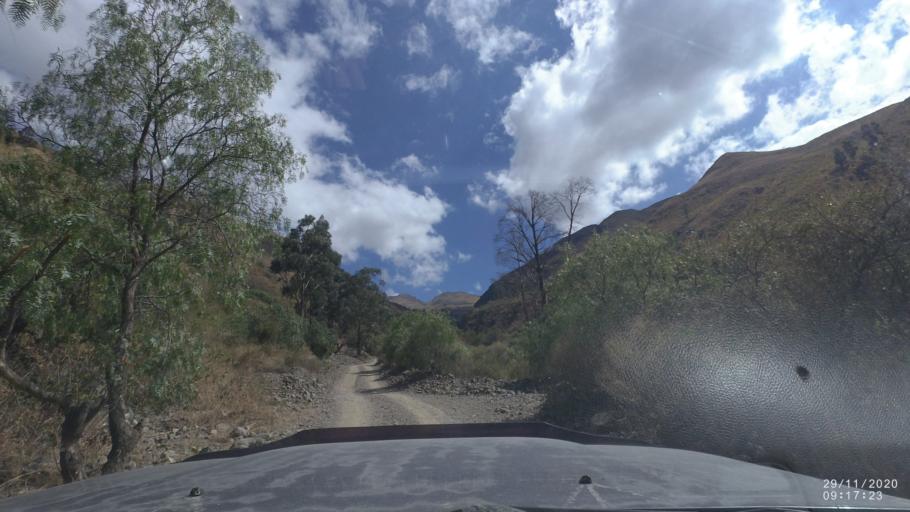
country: BO
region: Cochabamba
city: Cochabamba
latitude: -17.3244
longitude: -66.1840
